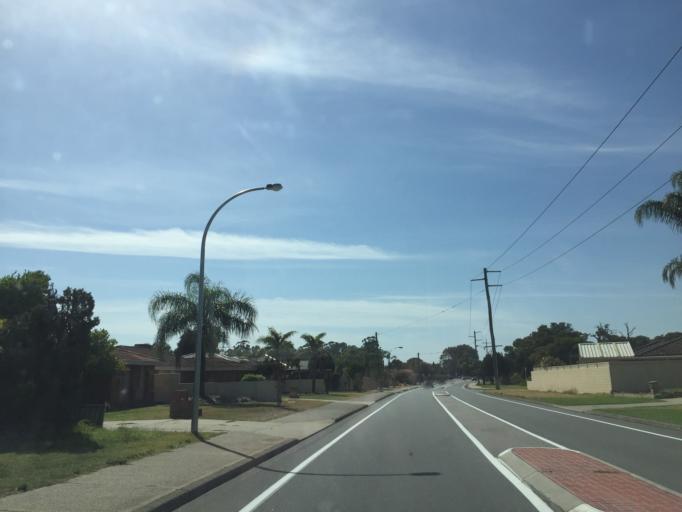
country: AU
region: Western Australia
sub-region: Gosnells
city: Thornlie
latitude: -32.0733
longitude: 115.9588
